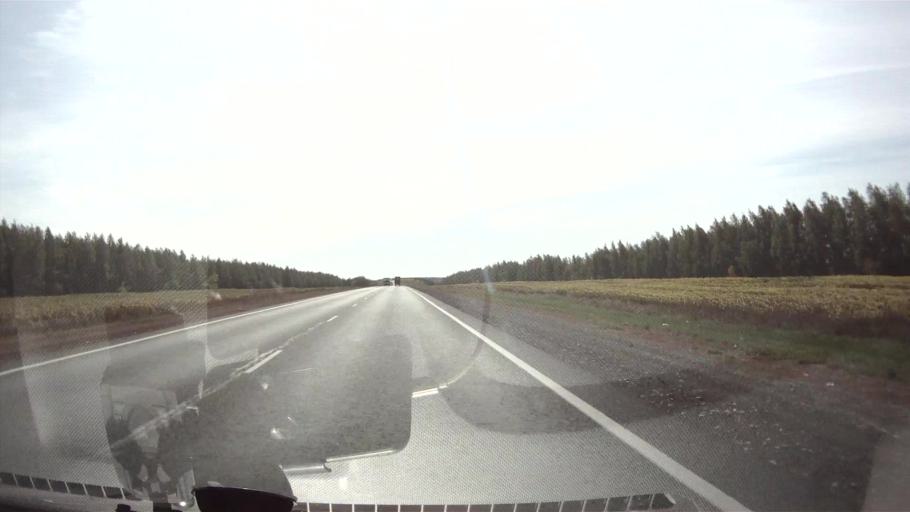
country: RU
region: Samara
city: Syzran'
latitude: 52.9093
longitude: 48.2991
